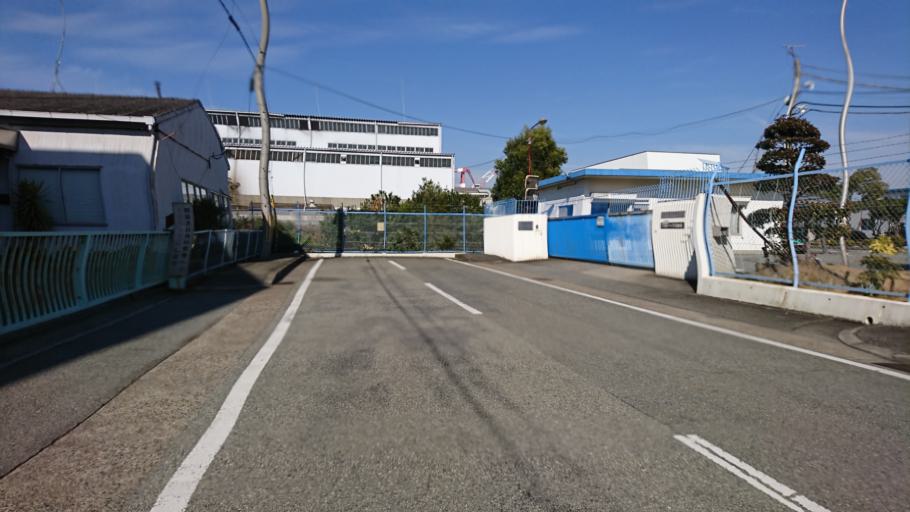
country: JP
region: Hyogo
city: Kakogawacho-honmachi
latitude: 34.6964
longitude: 134.8538
